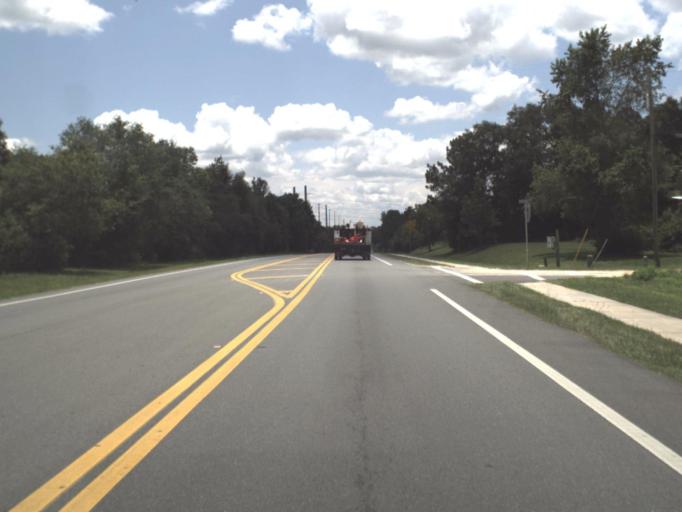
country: US
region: Florida
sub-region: Clay County
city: Keystone Heights
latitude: 29.7907
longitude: -82.0395
